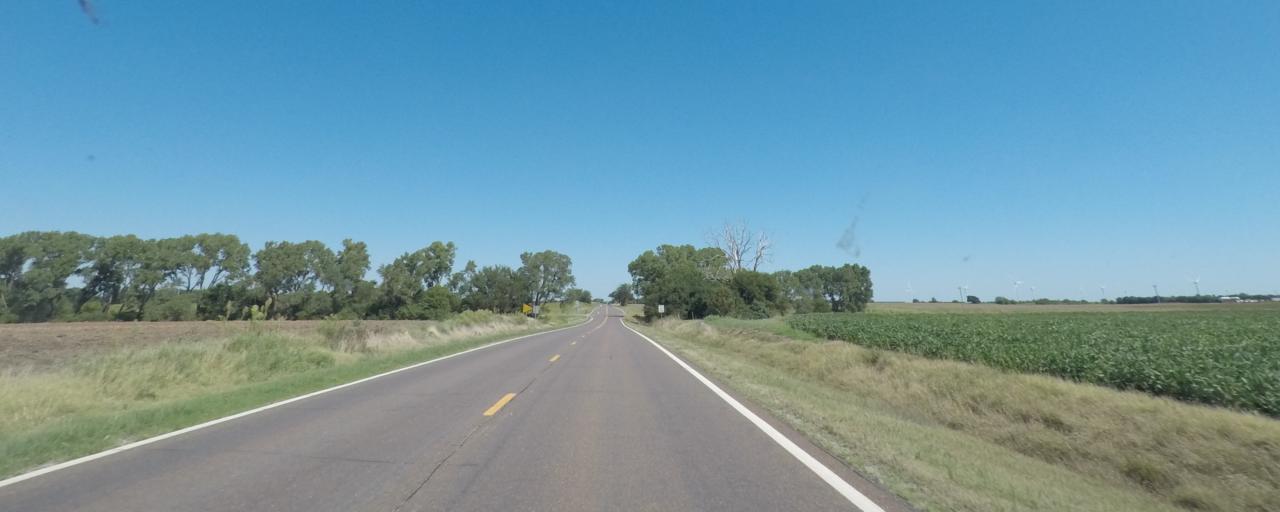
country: US
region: Kansas
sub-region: Sumner County
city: Wellington
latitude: 37.1127
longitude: -97.4016
